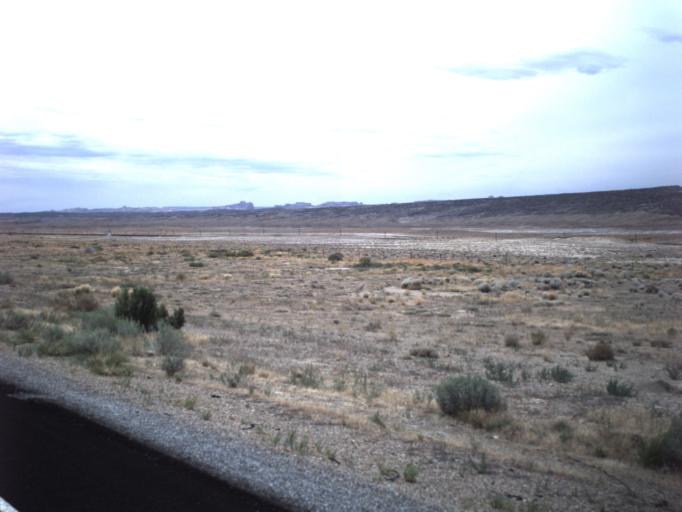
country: US
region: Utah
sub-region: Carbon County
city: East Carbon City
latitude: 39.1803
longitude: -110.3384
